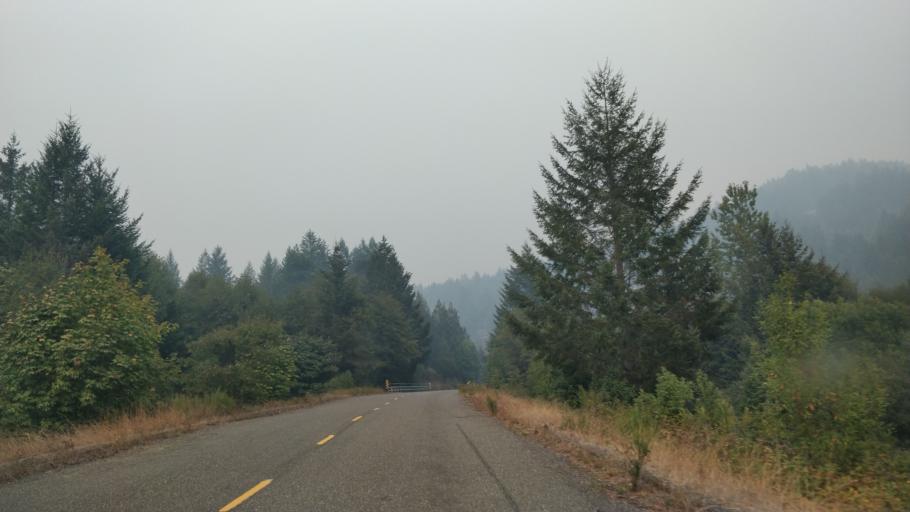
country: US
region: California
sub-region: Humboldt County
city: Rio Dell
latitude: 40.3325
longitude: -124.0281
